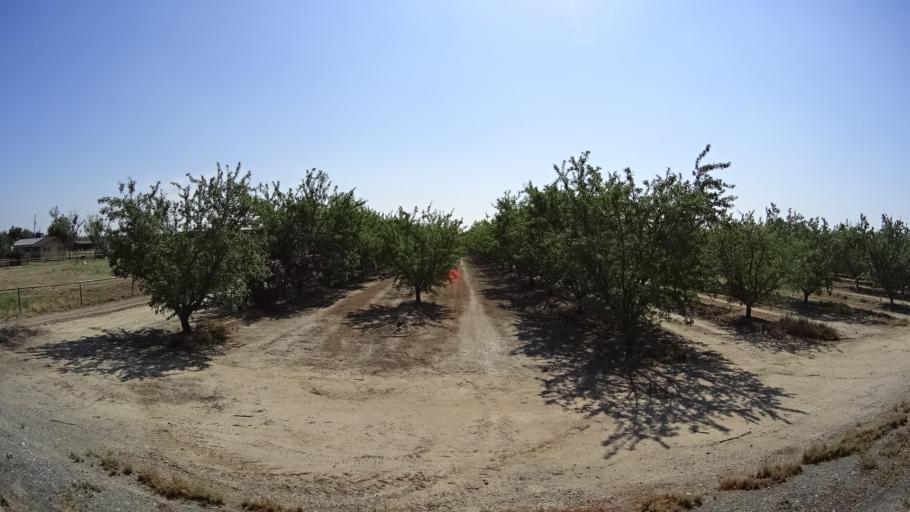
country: US
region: California
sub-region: Fresno County
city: Kingsburg
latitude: 36.4348
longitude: -119.5647
